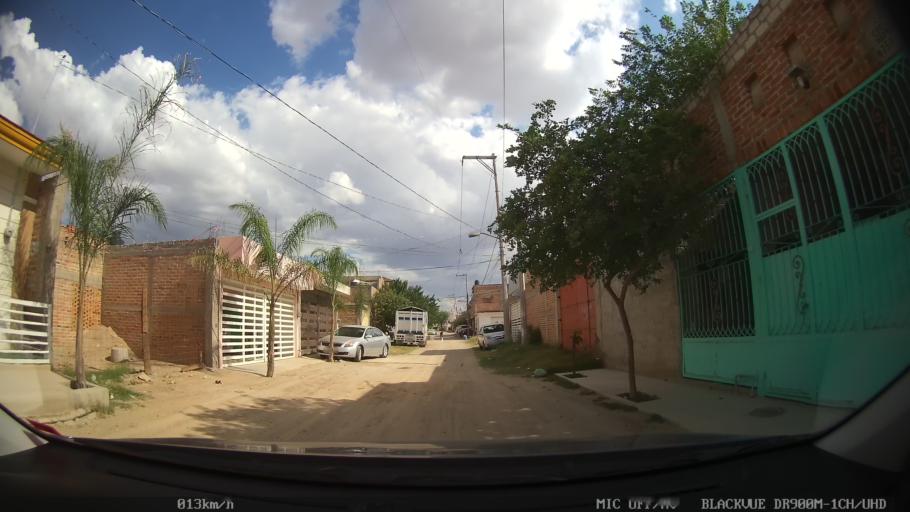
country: MX
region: Jalisco
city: Tlaquepaque
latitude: 20.6641
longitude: -103.2657
